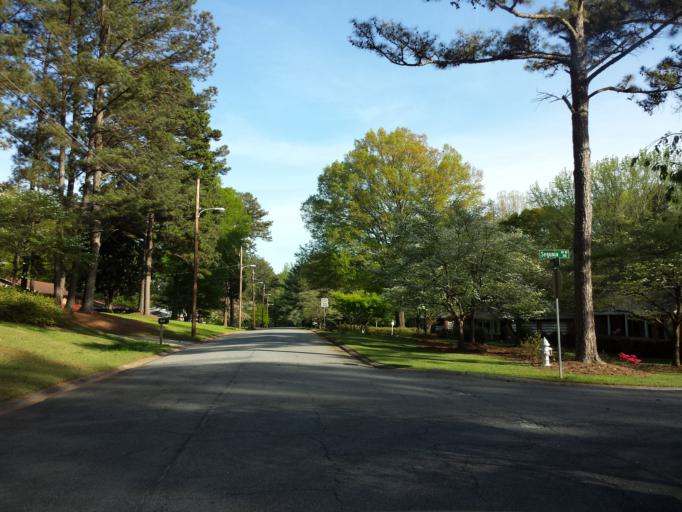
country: US
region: Georgia
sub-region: Cobb County
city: Marietta
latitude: 33.9706
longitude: -84.5421
